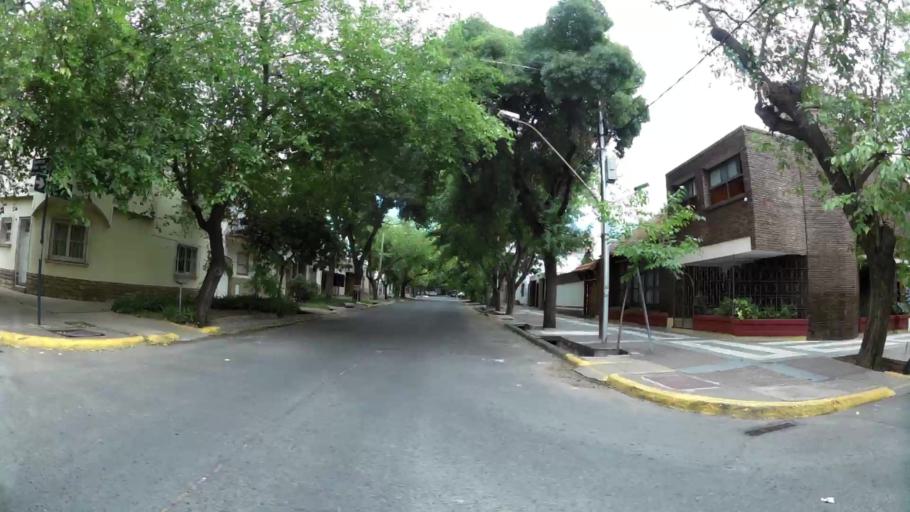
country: AR
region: Mendoza
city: Mendoza
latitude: -32.8931
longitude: -68.8570
